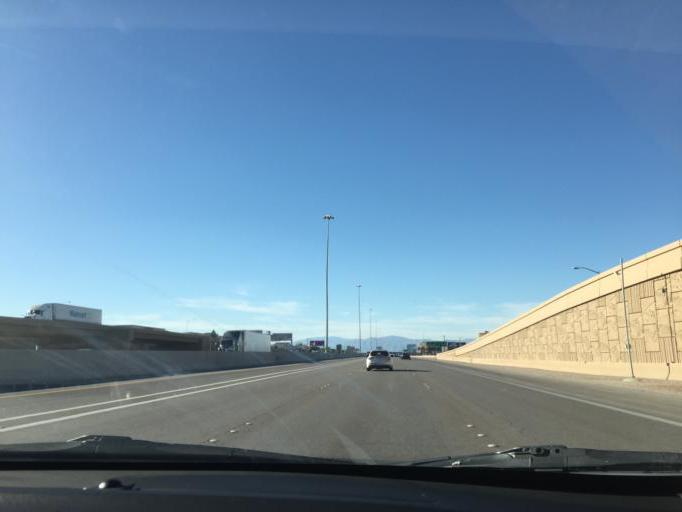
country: US
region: Nevada
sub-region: Clark County
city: Paradise
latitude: 36.0454
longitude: -115.1806
